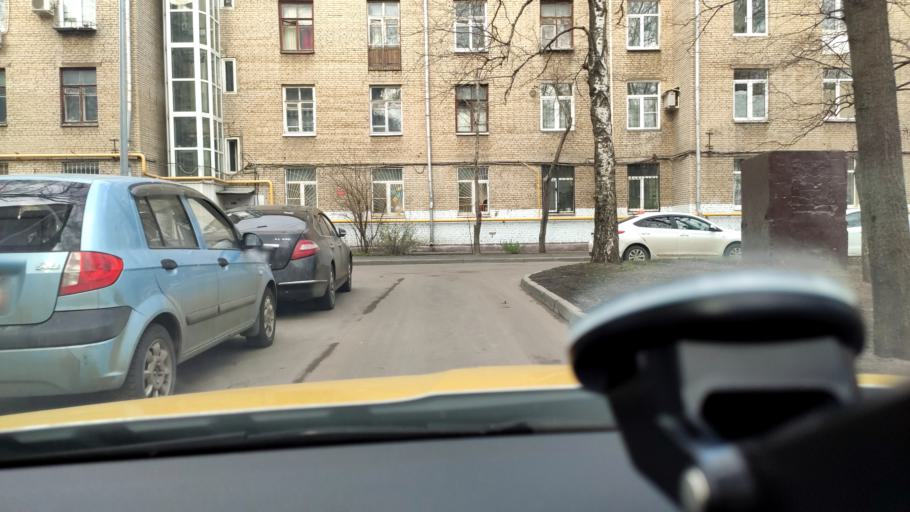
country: RU
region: Moscow
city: Leonovo
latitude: 55.8351
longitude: 37.6430
